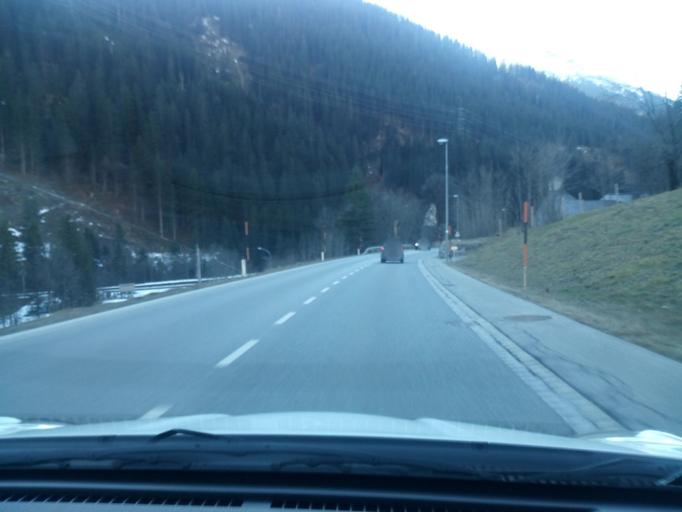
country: AT
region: Vorarlberg
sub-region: Politischer Bezirk Bludenz
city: Klosterle
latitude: 47.1330
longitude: 10.1246
